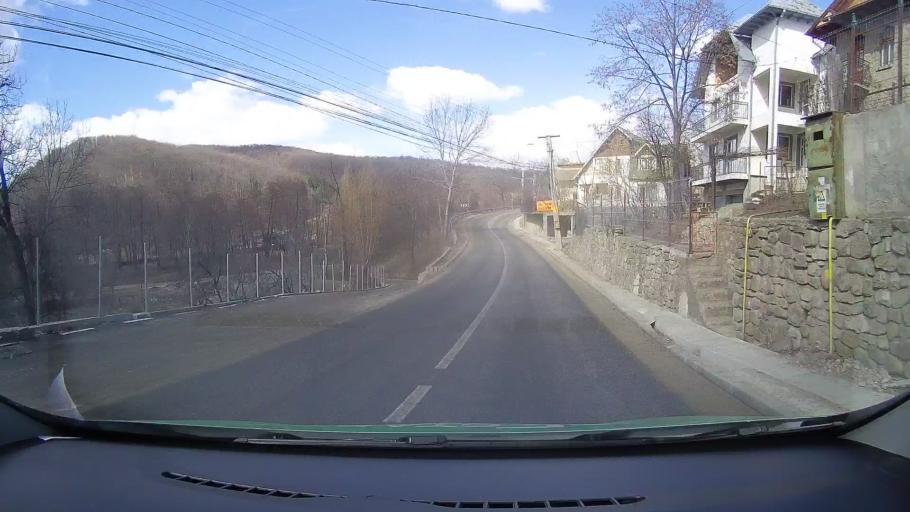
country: RO
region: Dambovita
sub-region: Comuna Fieni
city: Fieni
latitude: 45.1317
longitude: 25.4052
